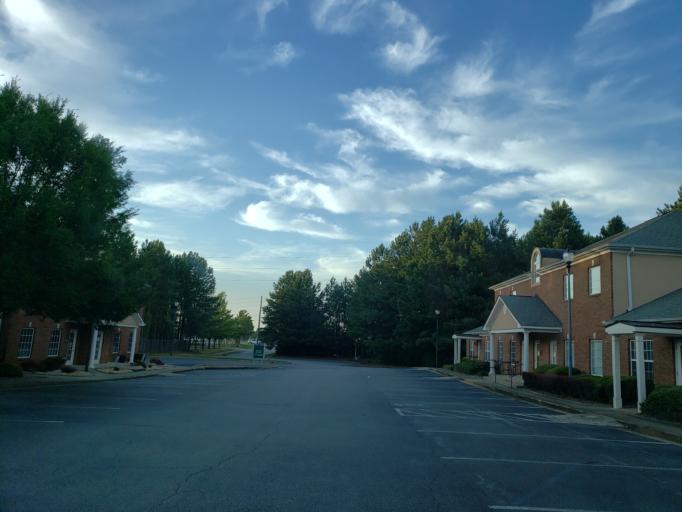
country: US
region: Georgia
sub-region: Cobb County
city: Kennesaw
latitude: 34.0463
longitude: -84.6020
